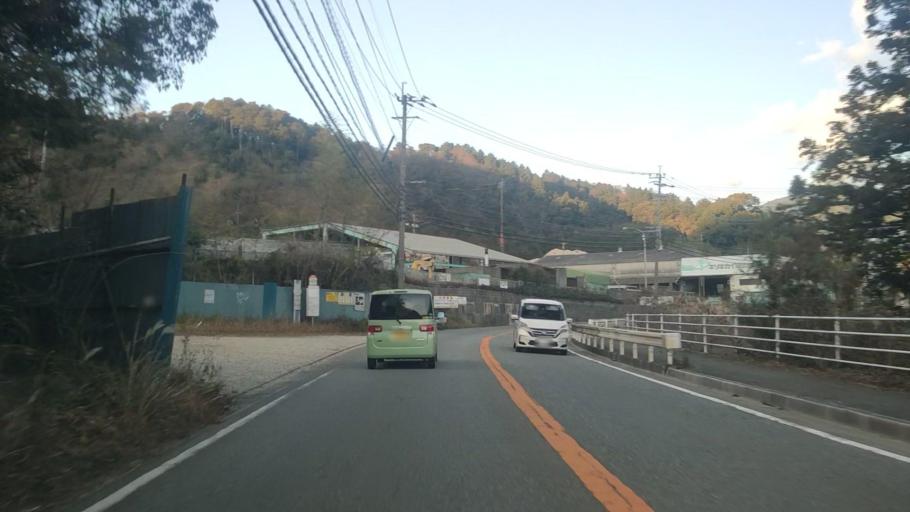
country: JP
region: Fukuoka
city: Dazaifu
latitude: 33.5441
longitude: 130.5390
